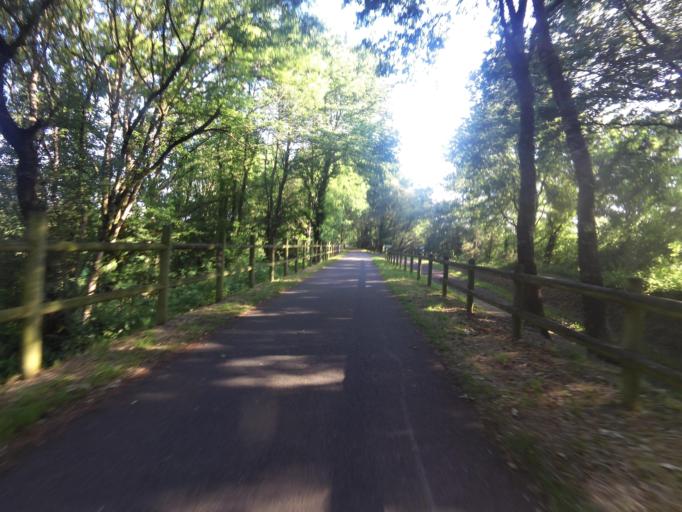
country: FR
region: Brittany
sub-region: Departement du Morbihan
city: Guillac
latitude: 47.8883
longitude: -2.4361
